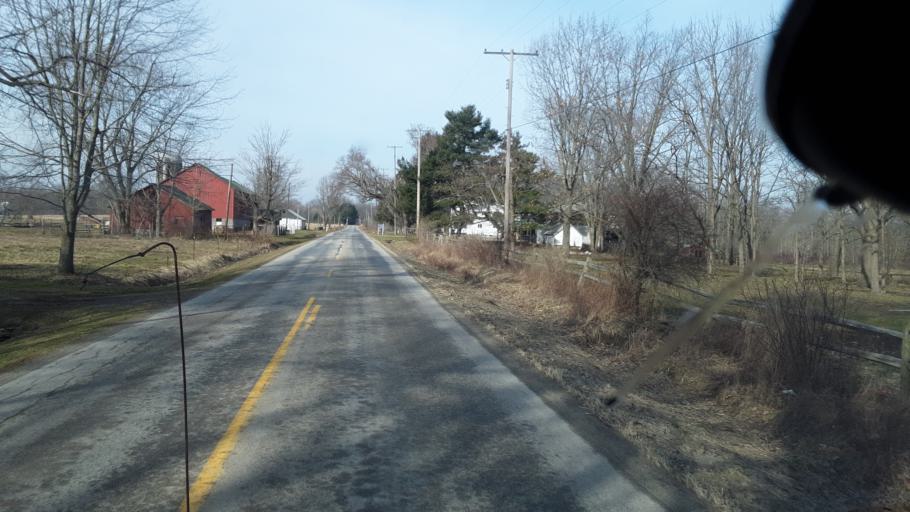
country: US
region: Ohio
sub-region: Ashtabula County
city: Jefferson
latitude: 41.7173
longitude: -80.6774
